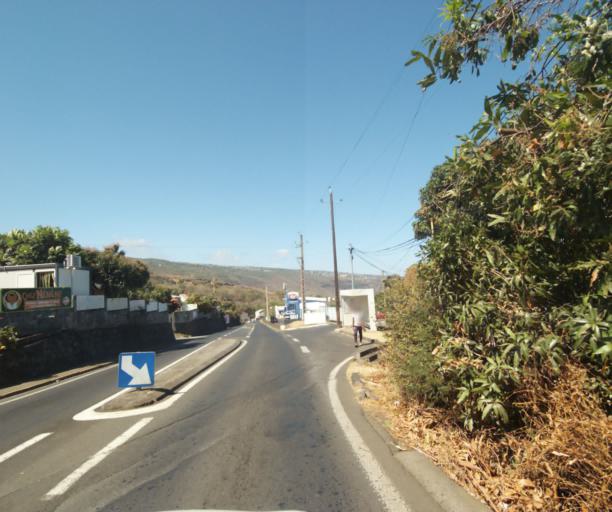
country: RE
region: Reunion
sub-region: Reunion
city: Le Port
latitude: -20.9783
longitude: 55.3183
